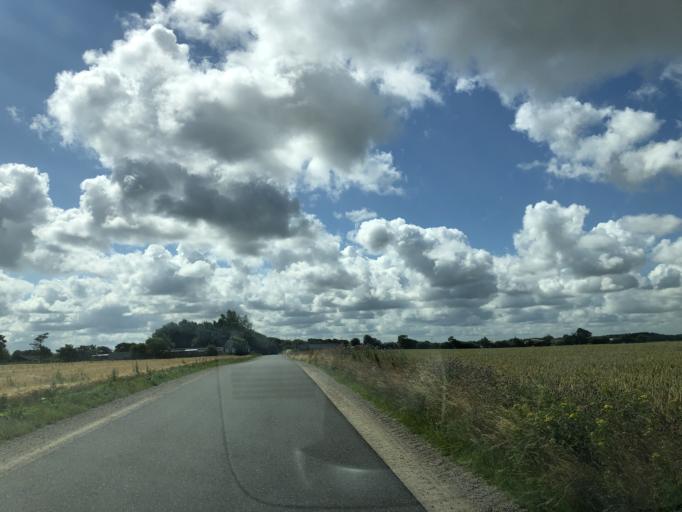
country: DK
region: Central Jutland
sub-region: Struer Kommune
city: Struer
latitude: 56.4691
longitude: 8.5215
